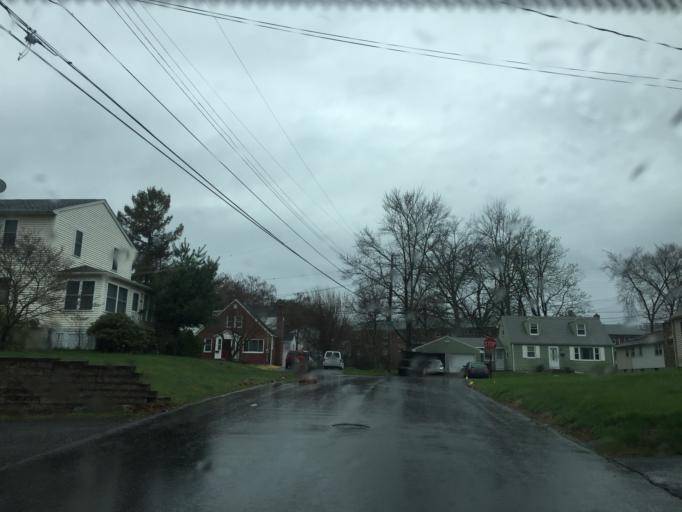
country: US
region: Connecticut
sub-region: Hartford County
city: New Britain
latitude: 41.6976
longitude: -72.7945
